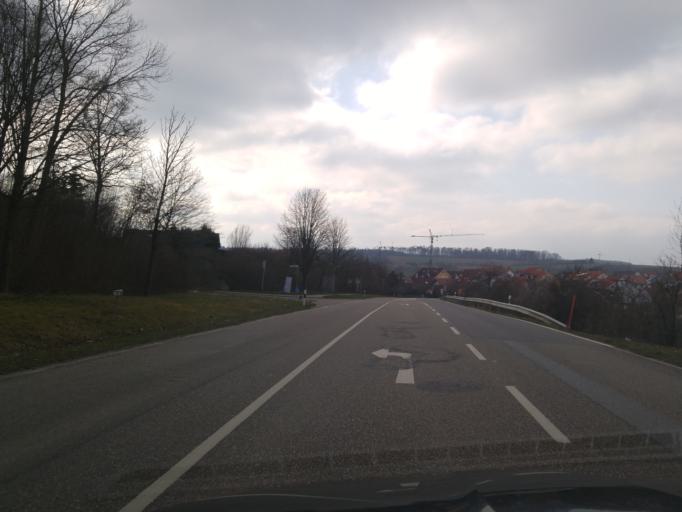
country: DE
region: Baden-Wuerttemberg
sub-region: Regierungsbezirk Stuttgart
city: Ilsfeld
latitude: 49.0594
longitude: 9.2388
